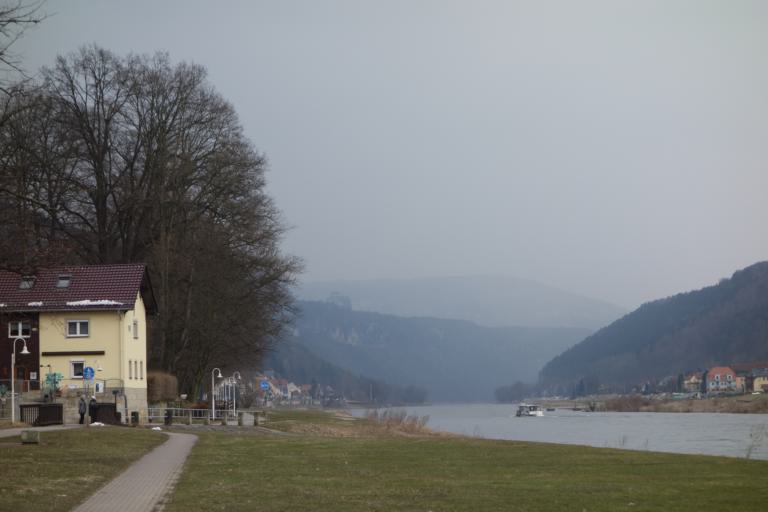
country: DE
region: Saxony
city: Bad Schandau
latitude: 50.9158
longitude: 14.1570
